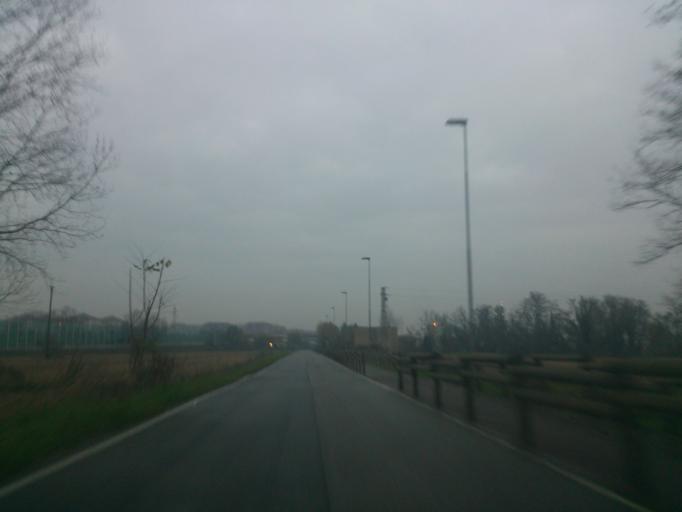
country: IT
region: Lombardy
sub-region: Citta metropolitana di Milano
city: San Donato Milanese
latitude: 45.4109
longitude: 9.2552
